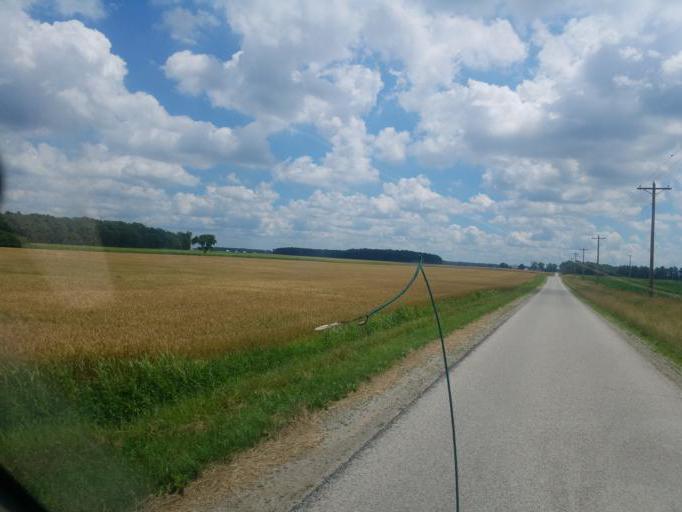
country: US
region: Ohio
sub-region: Huron County
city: Willard
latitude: 41.0224
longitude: -82.8305
